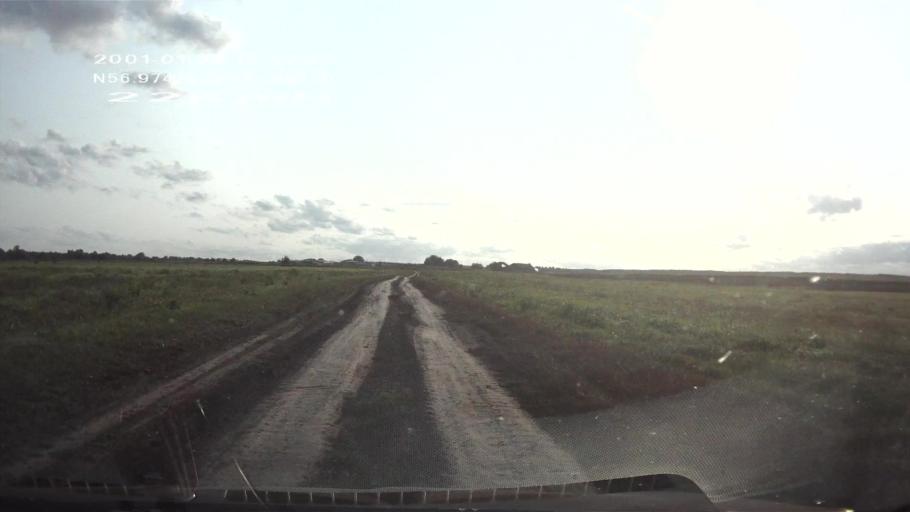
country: RU
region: Mariy-El
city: Kuzhener
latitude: 56.9740
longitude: 48.7952
